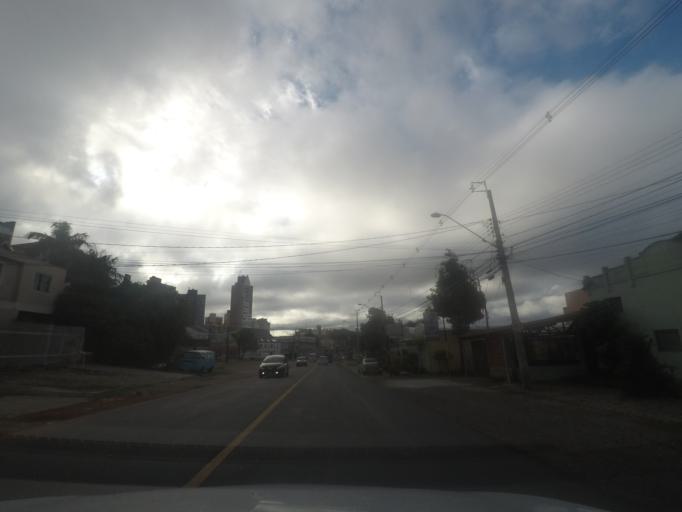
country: BR
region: Parana
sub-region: Curitiba
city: Curitiba
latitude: -25.4402
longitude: -49.2343
